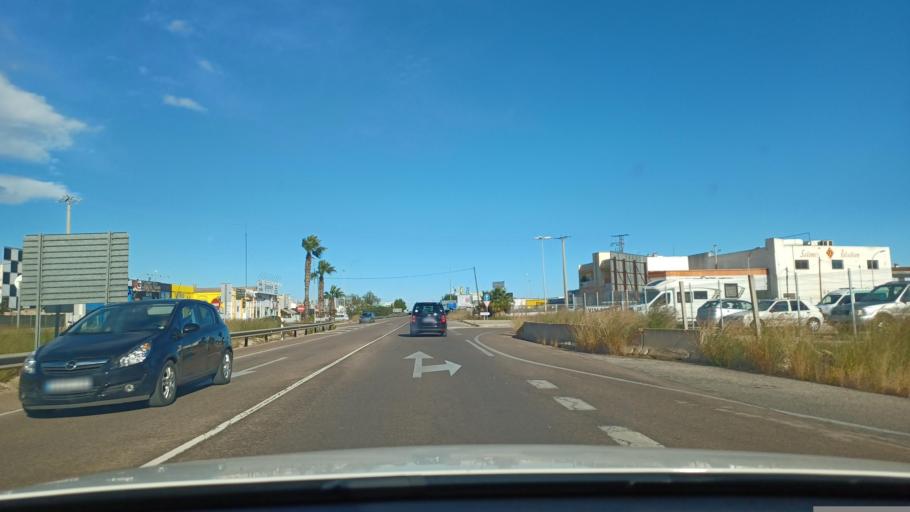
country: ES
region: Valencia
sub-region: Provincia de Castello
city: Vinaros
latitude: 40.4790
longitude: 0.4709
